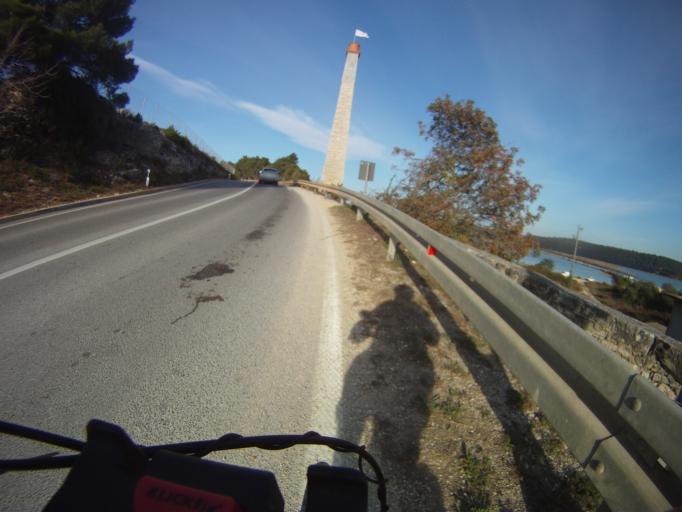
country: HR
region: Istarska
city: Novigrad
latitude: 45.3161
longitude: 13.5903
